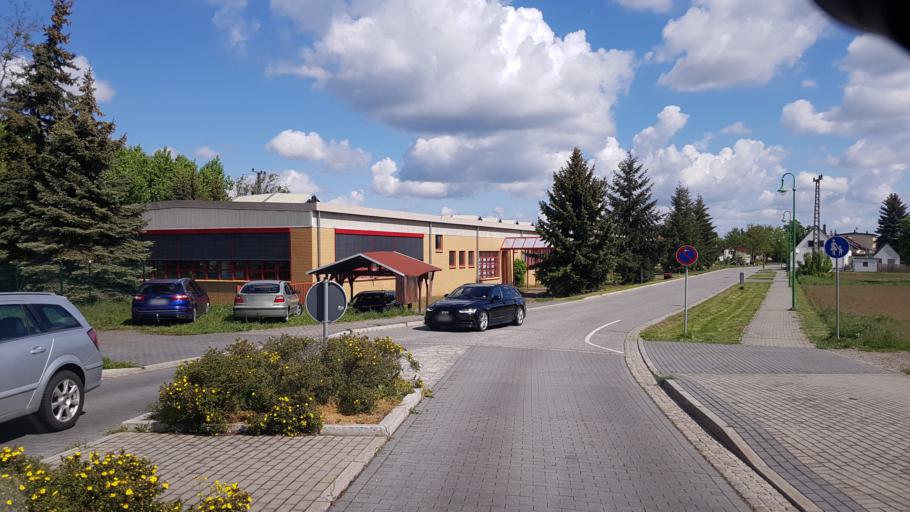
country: DE
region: Brandenburg
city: Grossraschen
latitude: 51.5791
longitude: 13.9994
